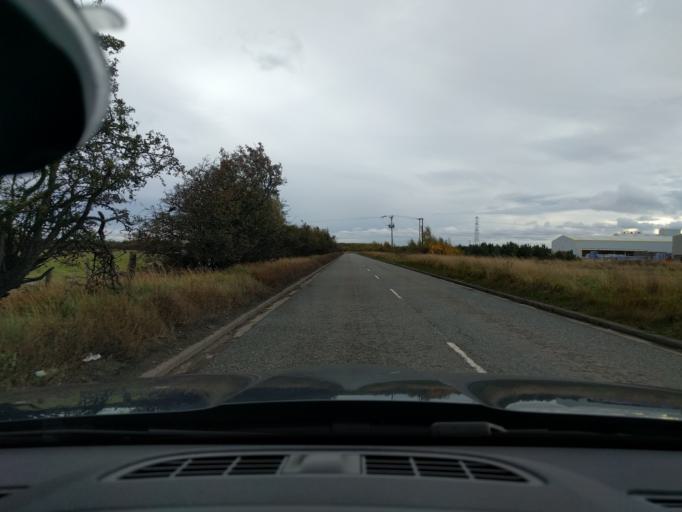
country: GB
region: England
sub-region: Northumberland
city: Ashington
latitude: 55.1540
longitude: -1.5526
